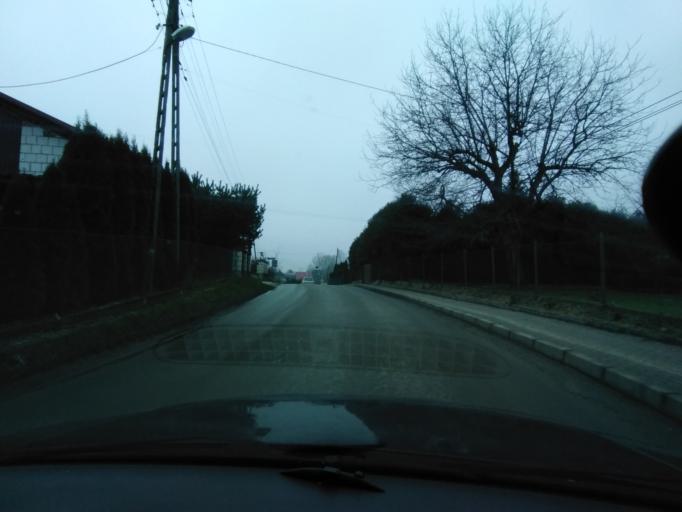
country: PL
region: Subcarpathian Voivodeship
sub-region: Powiat przeworski
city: Zarzecze
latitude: 49.9872
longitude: 22.5349
